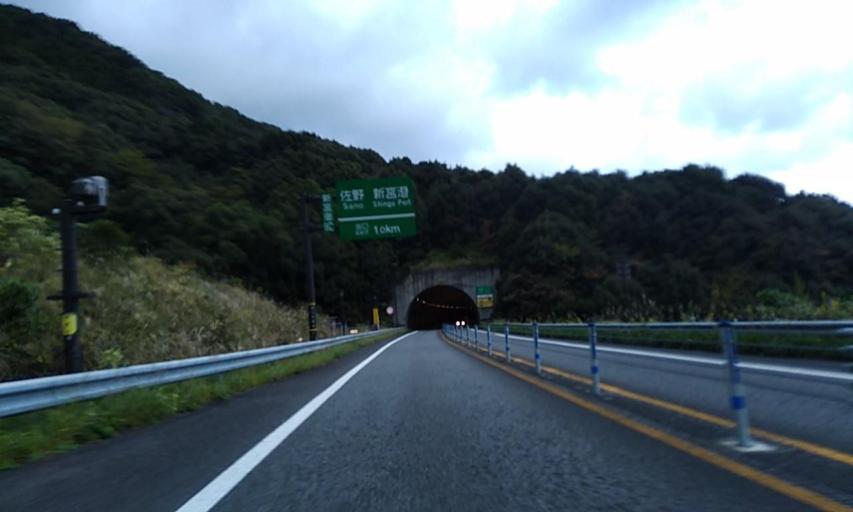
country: JP
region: Wakayama
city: Shingu
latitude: 33.6872
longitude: 135.9561
